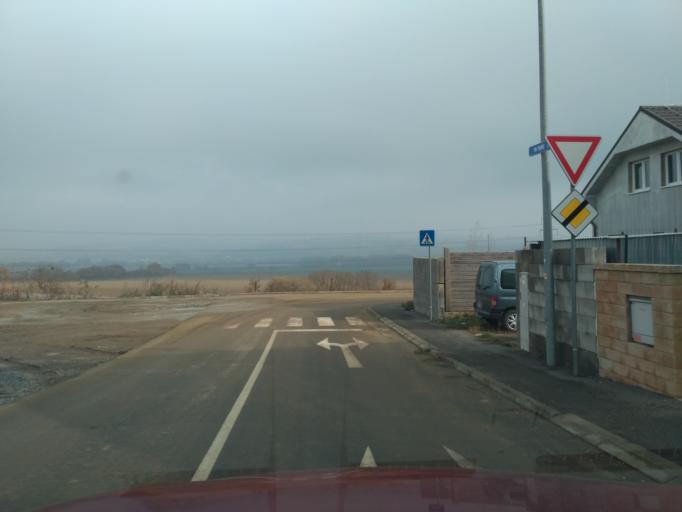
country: SK
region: Kosicky
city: Kosice
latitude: 48.6799
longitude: 21.3145
